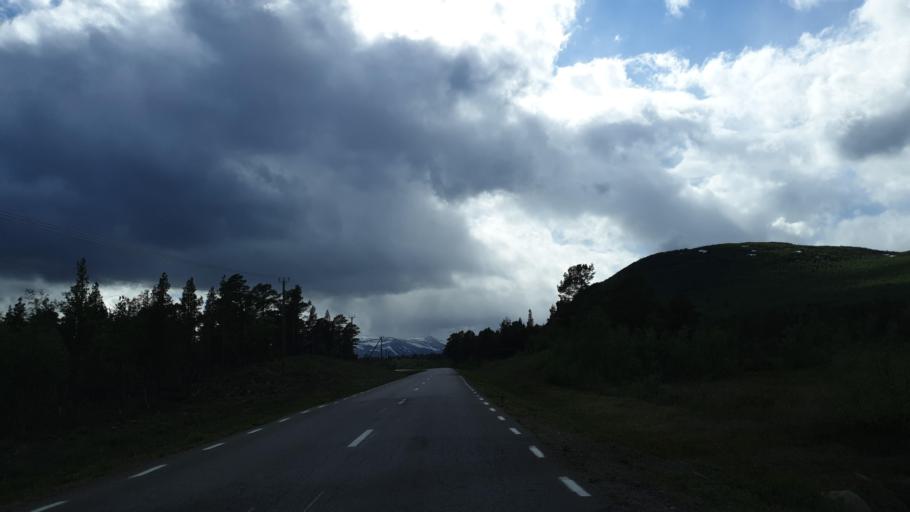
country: SE
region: Norrbotten
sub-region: Kiruna Kommun
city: Kiruna
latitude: 67.8737
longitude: 19.1777
